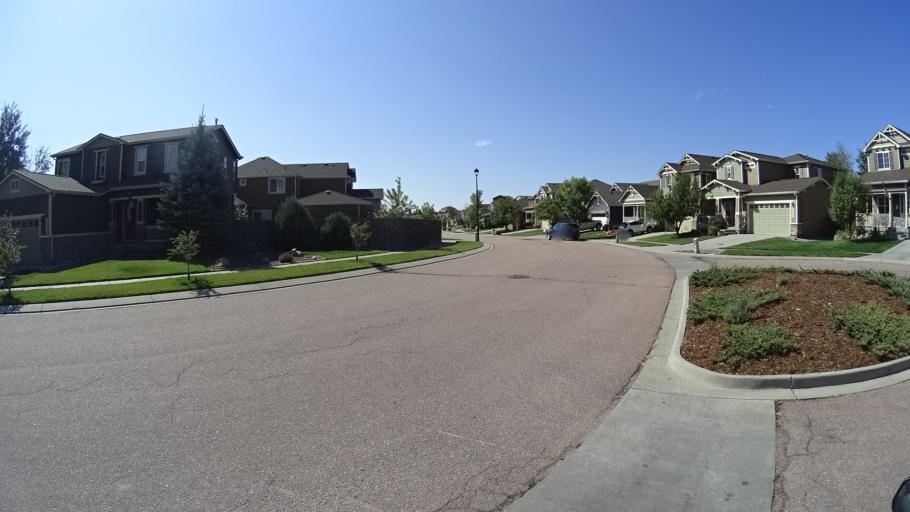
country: US
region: Colorado
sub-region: El Paso County
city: Cimarron Hills
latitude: 38.9295
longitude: -104.7049
